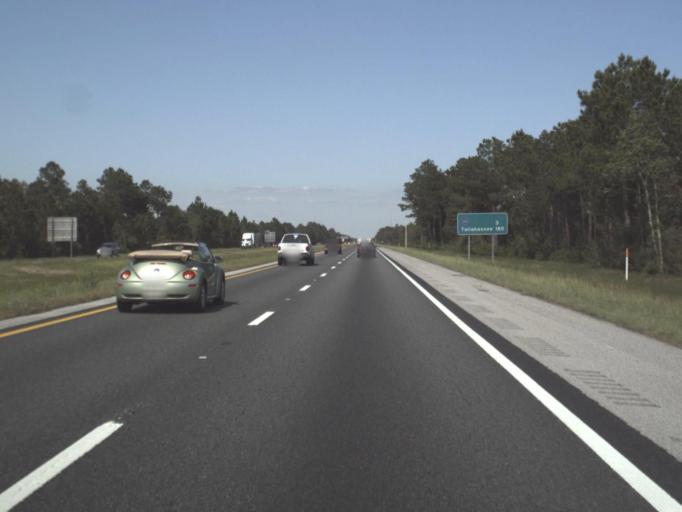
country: US
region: Florida
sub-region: Santa Rosa County
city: Bagdad
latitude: 30.5379
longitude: -87.0728
